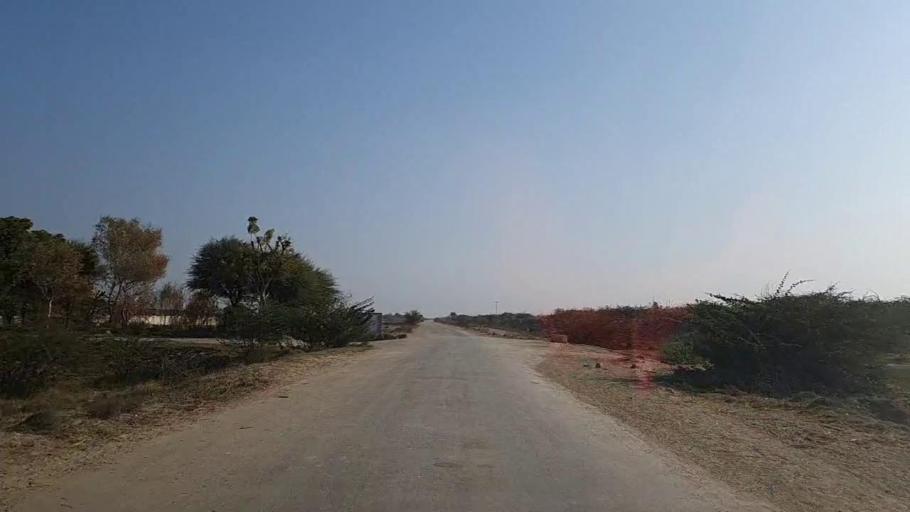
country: PK
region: Sindh
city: Tando Mittha Khan
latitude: 25.9271
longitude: 69.0655
